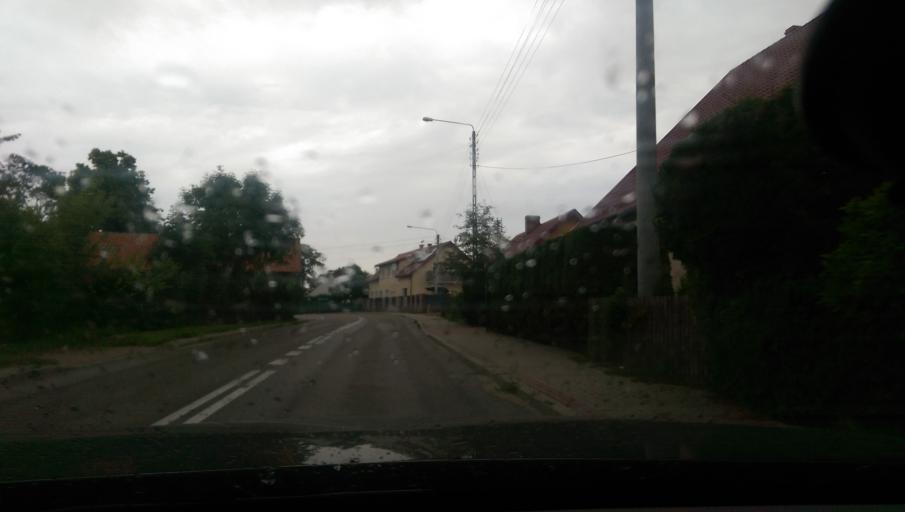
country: PL
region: Warmian-Masurian Voivodeship
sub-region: Powiat mragowski
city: Mikolajki
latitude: 53.8515
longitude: 21.6316
